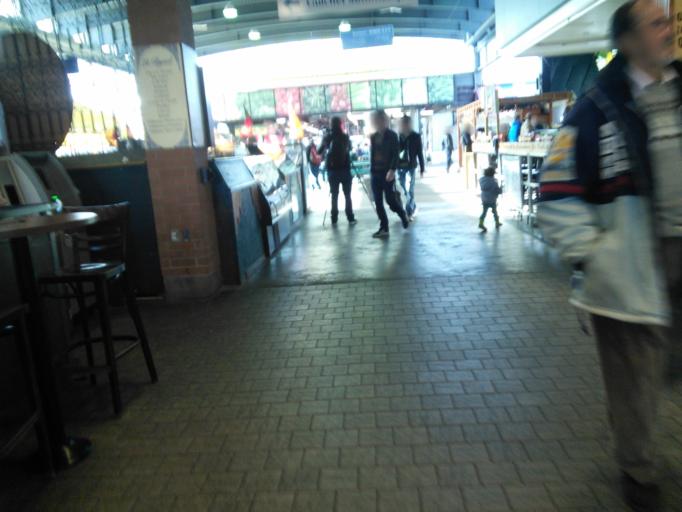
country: CA
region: Quebec
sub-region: Montreal
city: Montreal
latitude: 45.5366
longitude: -73.6145
